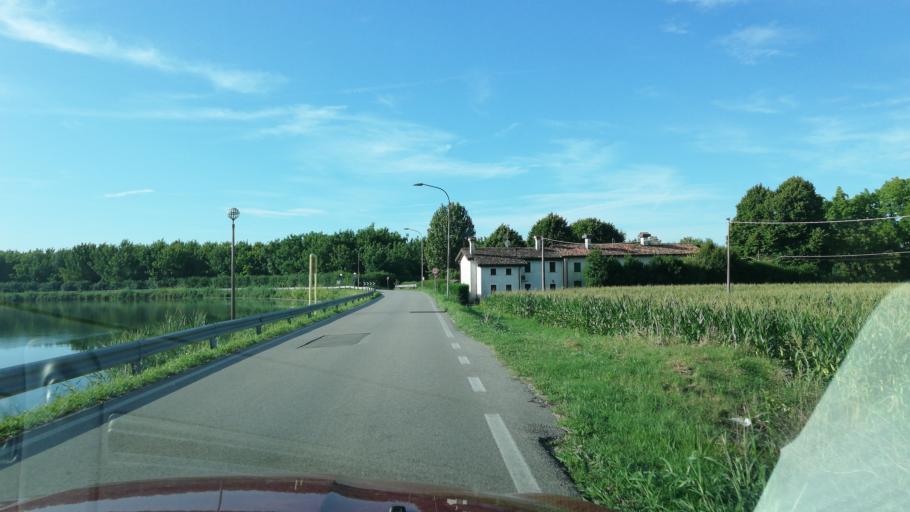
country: IT
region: Veneto
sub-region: Provincia di Venezia
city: San Giorgio di Livenza
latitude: 45.6416
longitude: 12.7903
